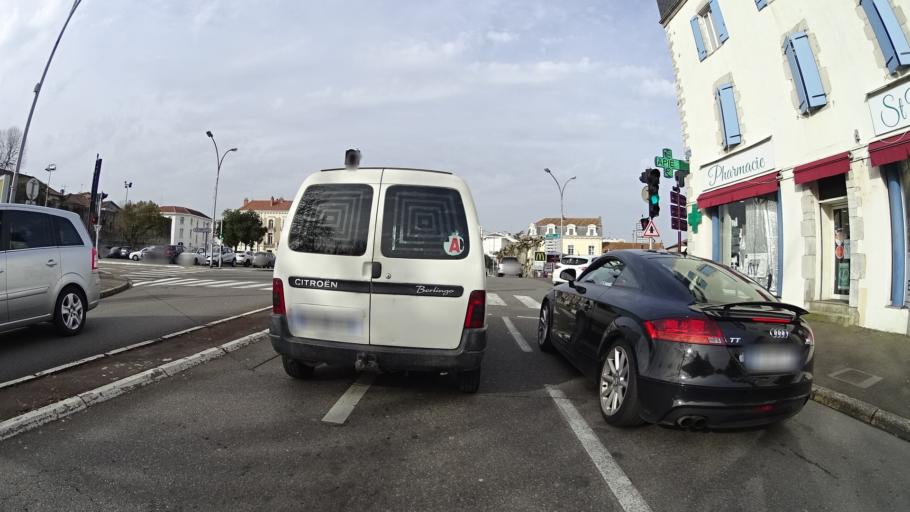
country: FR
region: Aquitaine
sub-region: Departement des Landes
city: Dax
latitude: 43.7086
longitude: -1.0499
